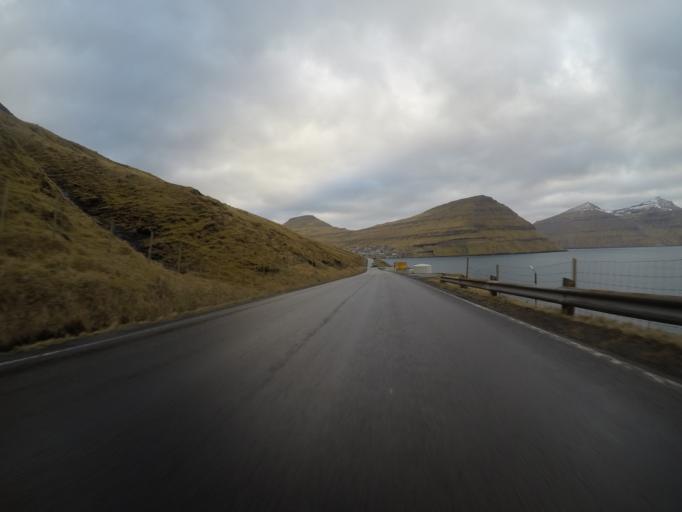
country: FO
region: Nordoyar
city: Klaksvik
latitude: 62.2486
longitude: -6.5831
